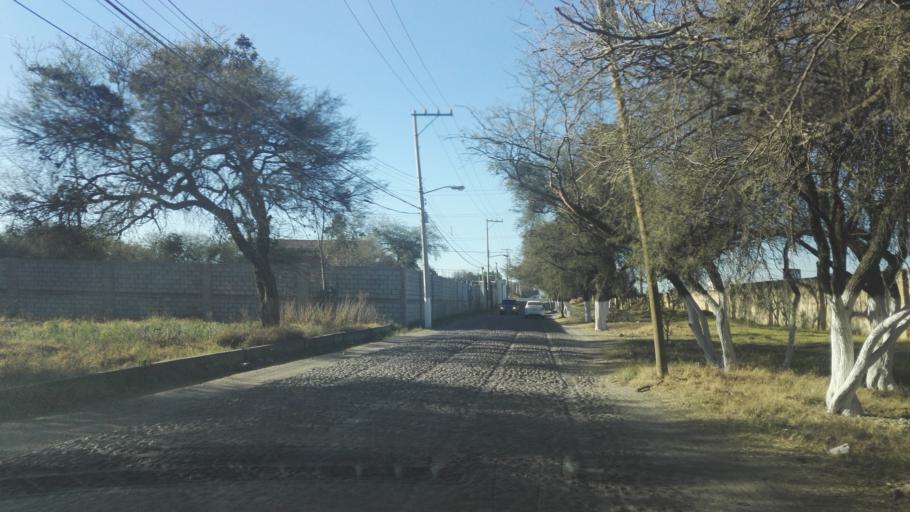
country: MX
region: Guanajuato
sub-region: Leon
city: Fraccionamiento Paraiso Real
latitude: 21.0710
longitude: -101.6002
